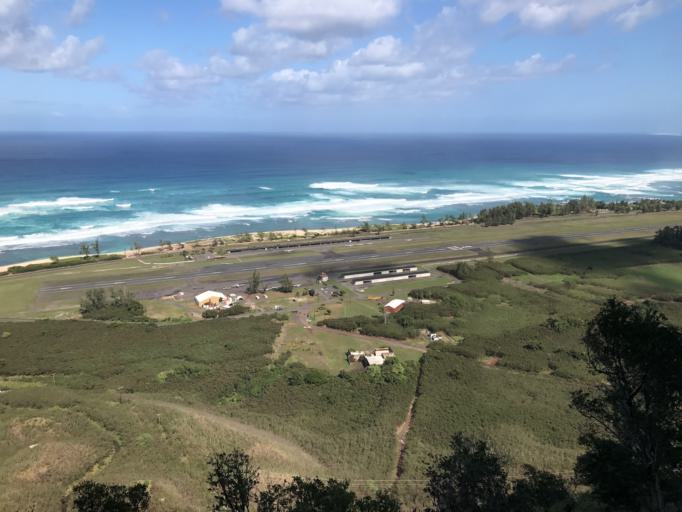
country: US
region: Hawaii
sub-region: Honolulu County
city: Mokuleia
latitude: 21.5729
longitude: -158.2101
